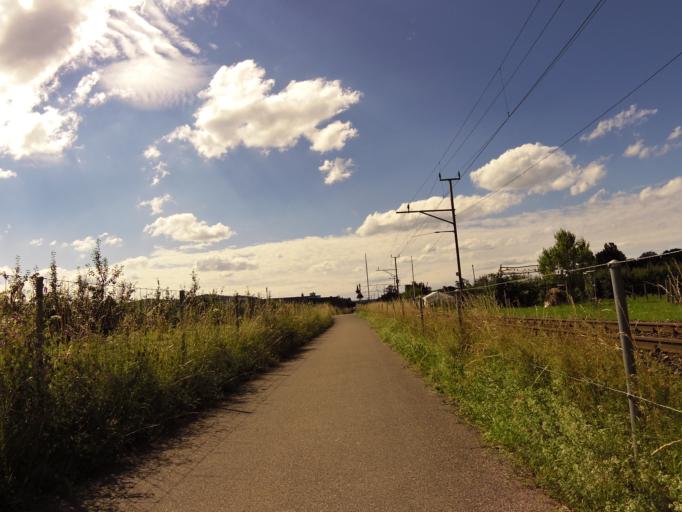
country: CH
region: Thurgau
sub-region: Arbon District
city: Egnach
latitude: 47.5416
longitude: 9.3888
